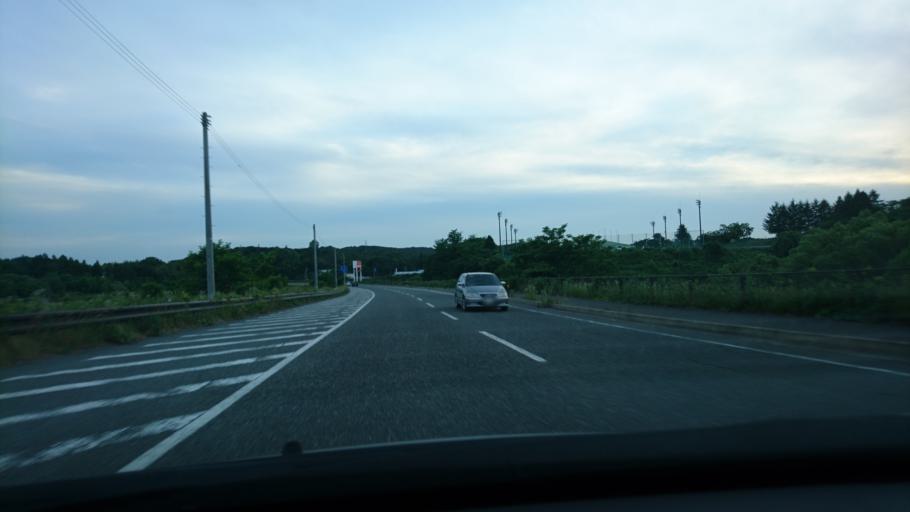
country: JP
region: Miyagi
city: Furukawa
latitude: 38.7244
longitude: 141.0280
